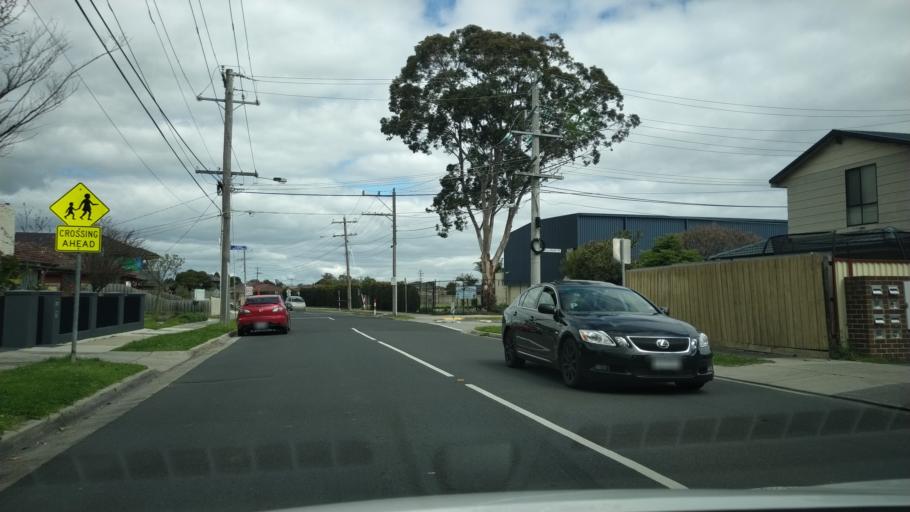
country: AU
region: Victoria
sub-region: Greater Dandenong
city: Keysborough
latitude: -37.9792
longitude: 145.1718
